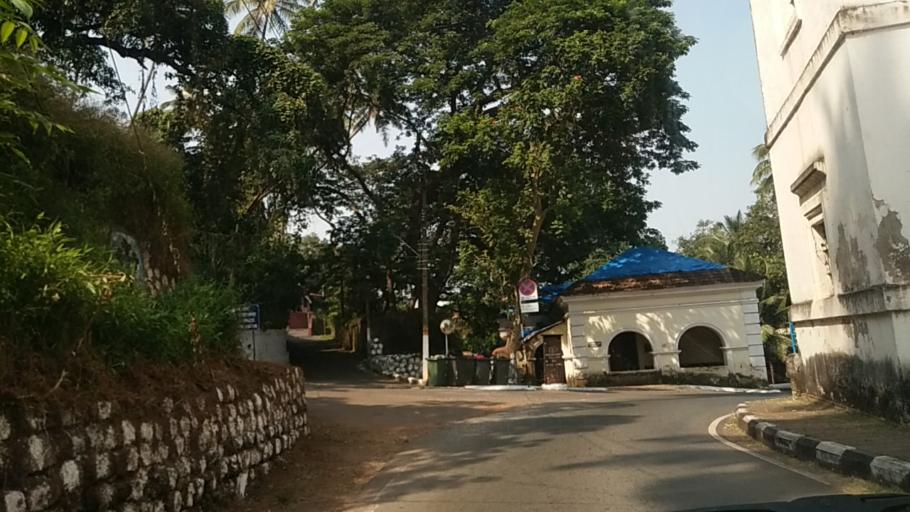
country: IN
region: Goa
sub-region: North Goa
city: Panaji
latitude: 15.5054
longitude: 73.8653
